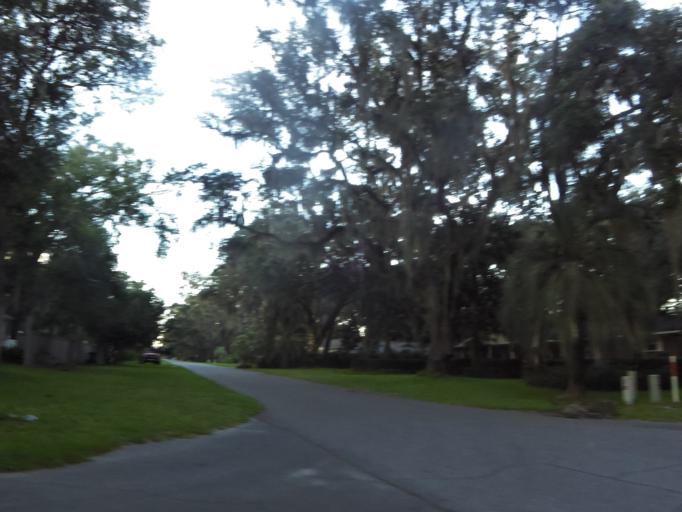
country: US
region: Georgia
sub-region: Camden County
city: St. Marys
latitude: 30.7242
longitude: -81.5567
